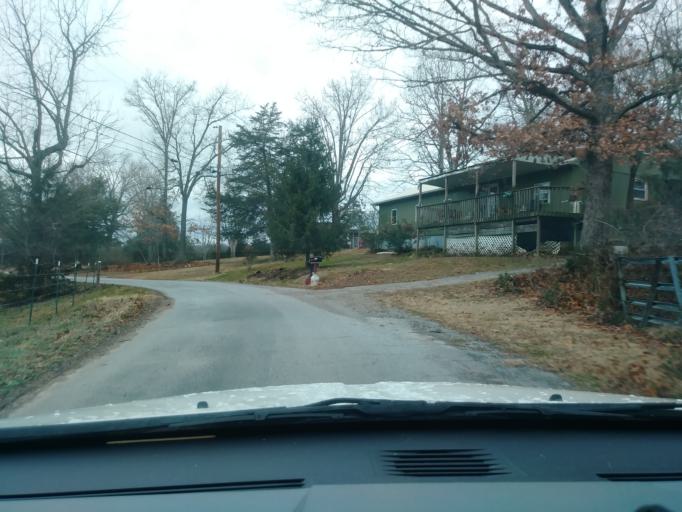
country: US
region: Tennessee
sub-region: Greene County
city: Greeneville
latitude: 36.1018
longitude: -82.8852
